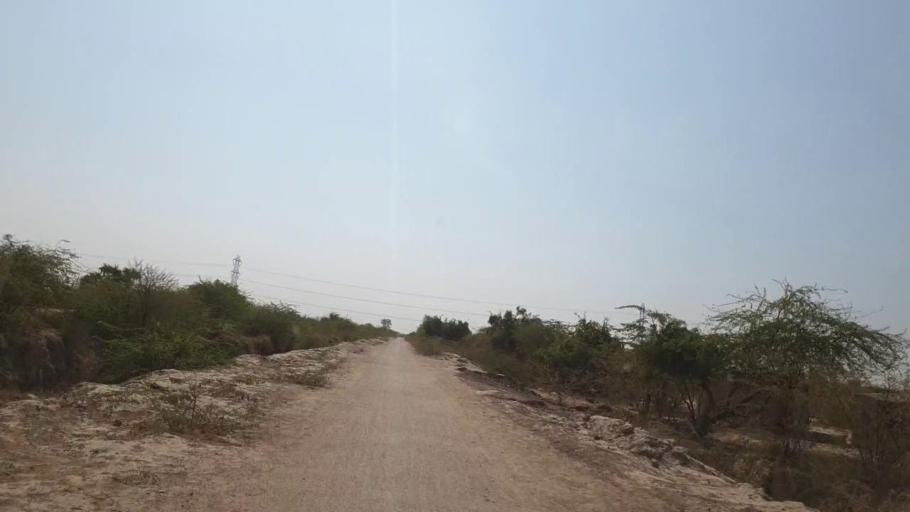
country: PK
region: Sindh
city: Nabisar
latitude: 25.0666
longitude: 69.5379
